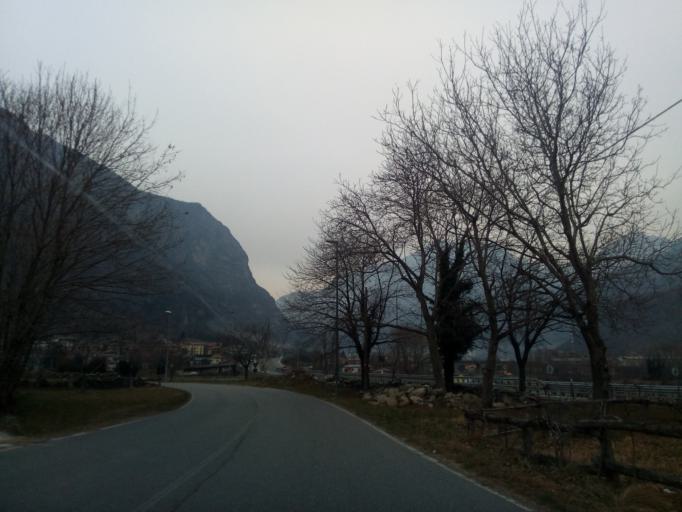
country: IT
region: Piedmont
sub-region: Provincia di Torino
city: Quincinetto
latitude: 45.5604
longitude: 7.8133
